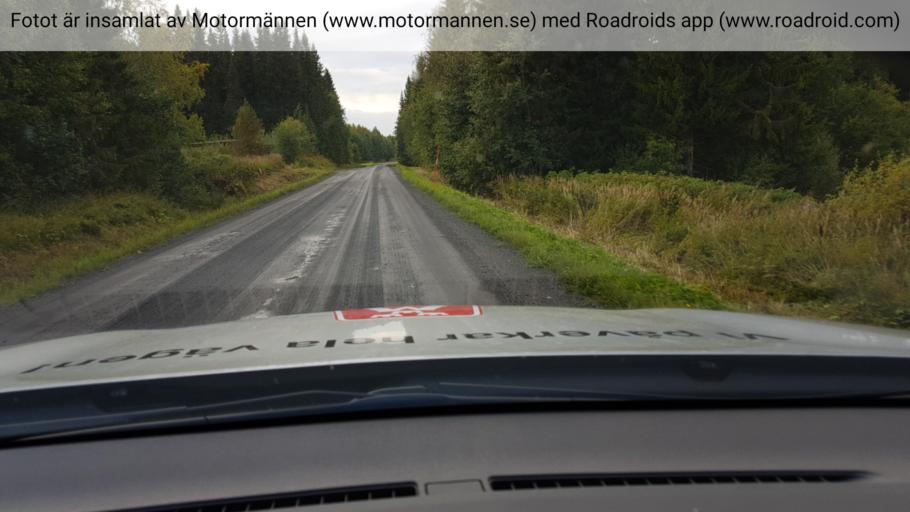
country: SE
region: Jaemtland
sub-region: Stroemsunds Kommun
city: Stroemsund
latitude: 64.1367
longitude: 15.7583
